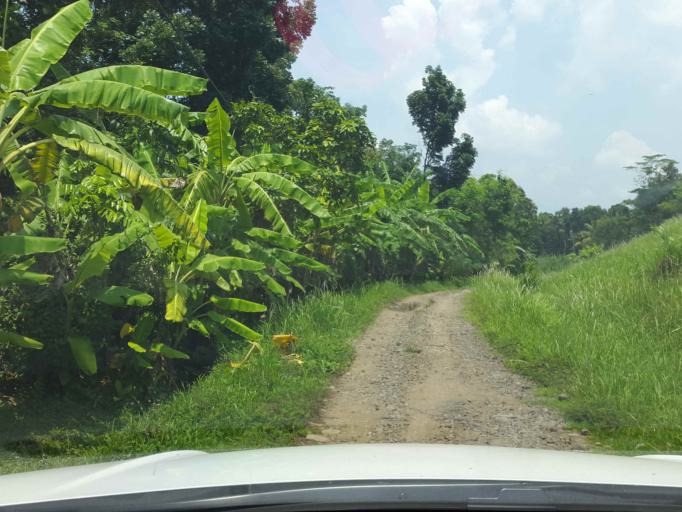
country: ID
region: Central Java
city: Winangun
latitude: -7.3654
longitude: 108.6924
